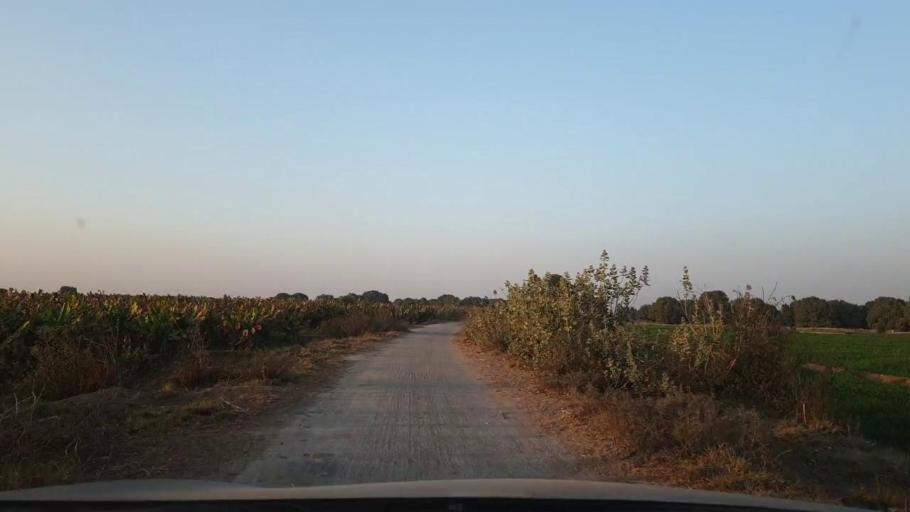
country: PK
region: Sindh
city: Tando Allahyar
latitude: 25.5260
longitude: 68.7354
